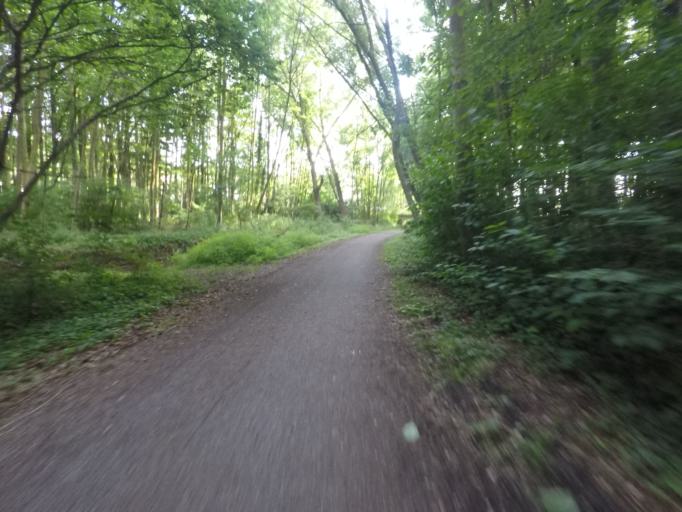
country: DE
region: North Rhine-Westphalia
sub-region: Regierungsbezirk Detmold
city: Hiddenhausen
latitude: 52.1648
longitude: 8.6013
